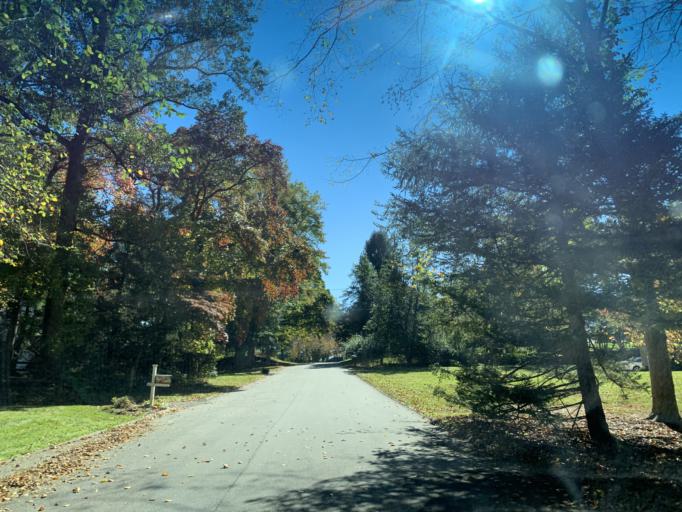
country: US
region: Maryland
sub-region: Harford County
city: Bel Air South
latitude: 39.5190
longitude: -76.3225
